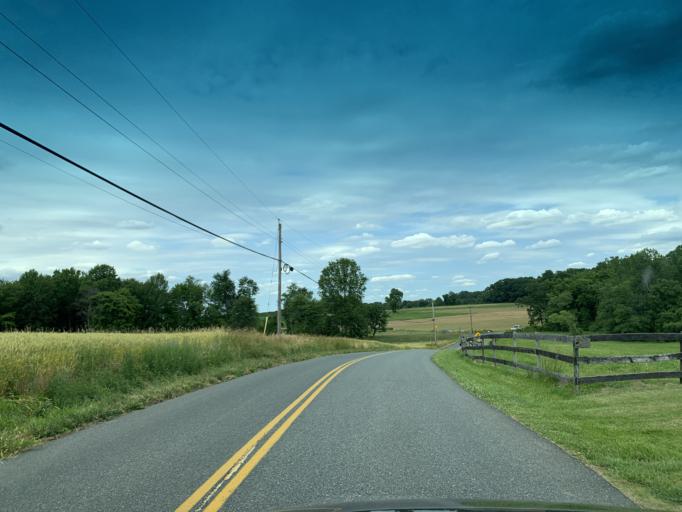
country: US
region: Maryland
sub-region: Harford County
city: Jarrettsville
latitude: 39.6126
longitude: -76.4990
